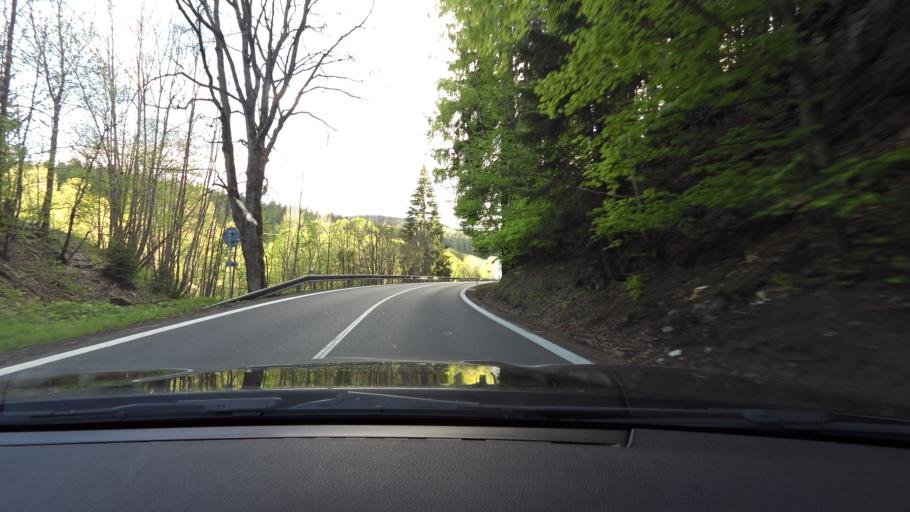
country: CZ
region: Plzensky
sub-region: Okres Klatovy
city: Zelezna Ruda
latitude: 49.1304
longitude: 13.2189
